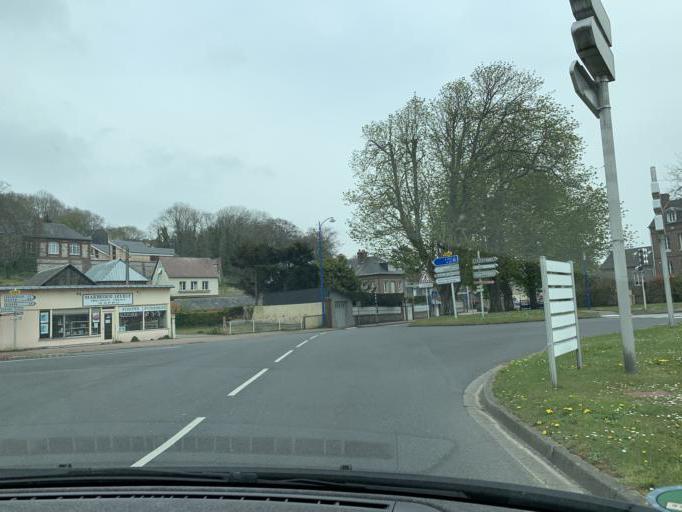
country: FR
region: Haute-Normandie
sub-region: Departement de la Seine-Maritime
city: Saint-Valery-en-Caux
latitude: 49.8627
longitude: 0.7132
